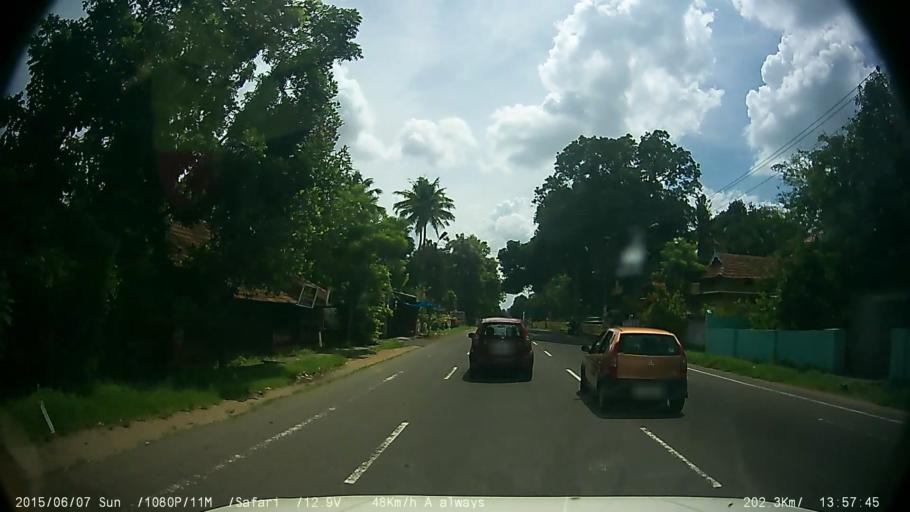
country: IN
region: Kerala
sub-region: Ernakulam
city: Angamali
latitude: 10.1835
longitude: 76.4080
